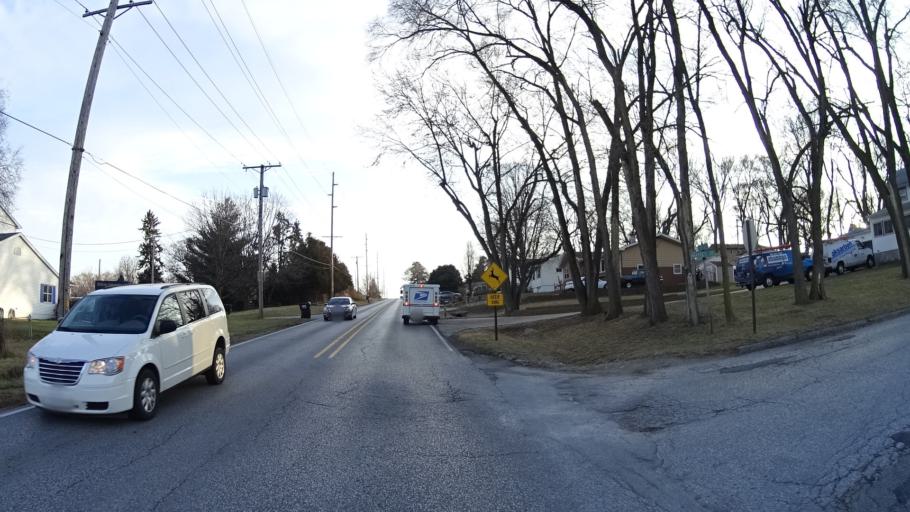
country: US
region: Nebraska
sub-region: Sarpy County
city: La Vista
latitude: 41.1739
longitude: -95.9673
